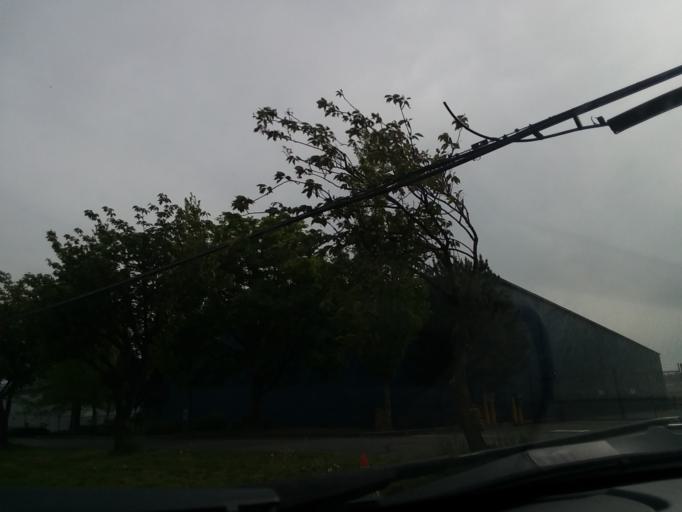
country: US
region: Washington
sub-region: King County
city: Boulevard Park
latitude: 47.5316
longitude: -122.2971
